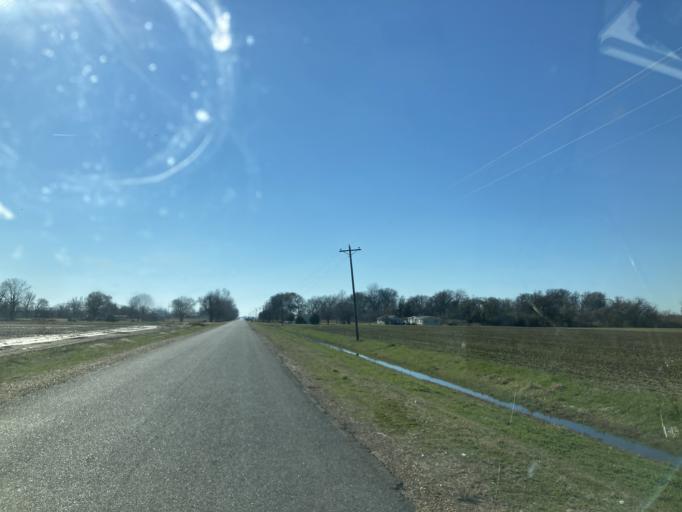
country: US
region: Mississippi
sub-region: Yazoo County
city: Yazoo City
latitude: 32.9720
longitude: -90.5950
